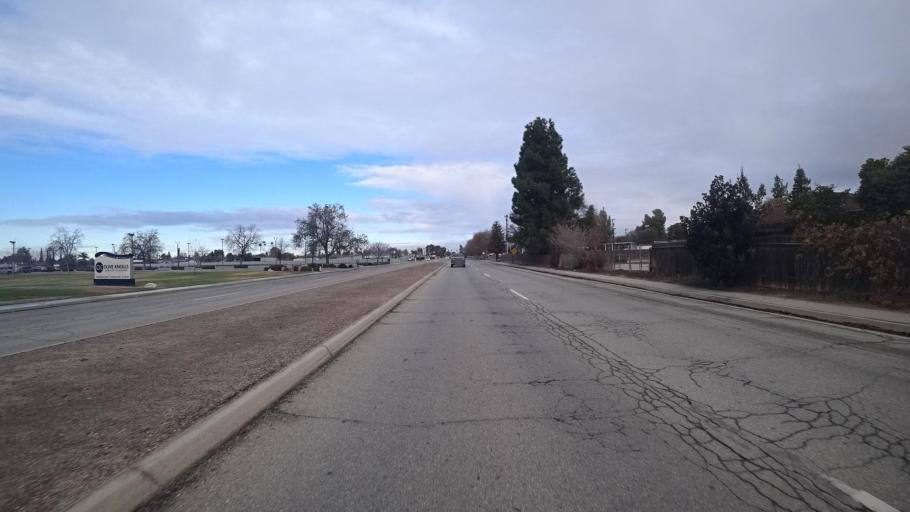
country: US
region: California
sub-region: Kern County
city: Greenacres
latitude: 35.4171
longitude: -119.0745
